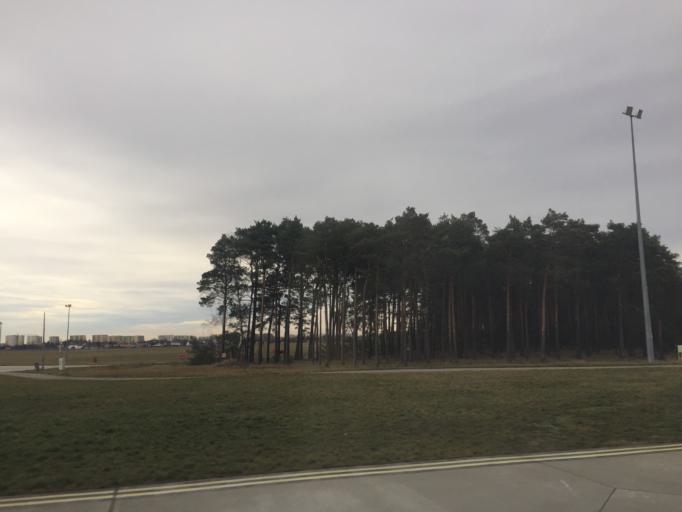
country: PL
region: Kujawsko-Pomorskie
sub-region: Bydgoszcz
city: Bydgoszcz
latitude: 53.0951
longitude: 17.9968
